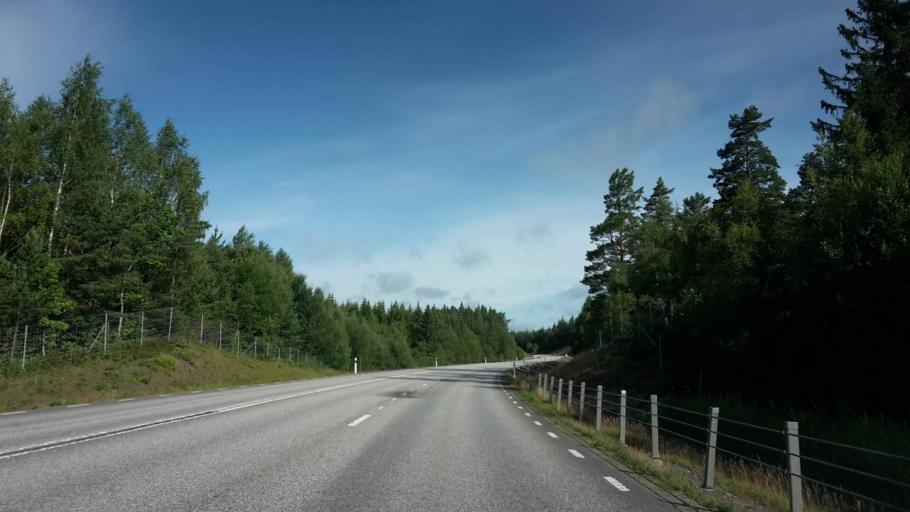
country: SE
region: OEstergoetland
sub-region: Motala Kommun
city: Borensberg
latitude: 58.5655
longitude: 15.3048
